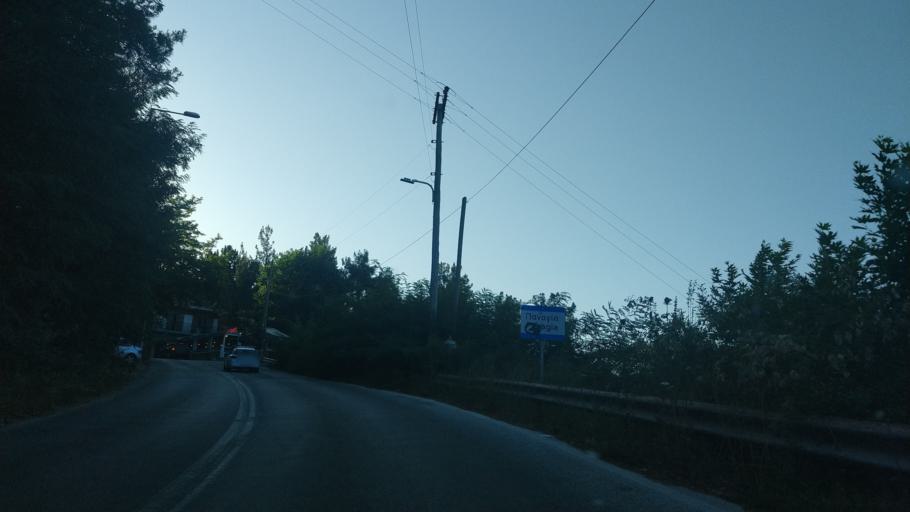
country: GR
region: East Macedonia and Thrace
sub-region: Nomos Kavalas
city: Potamia
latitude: 40.7291
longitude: 24.7322
